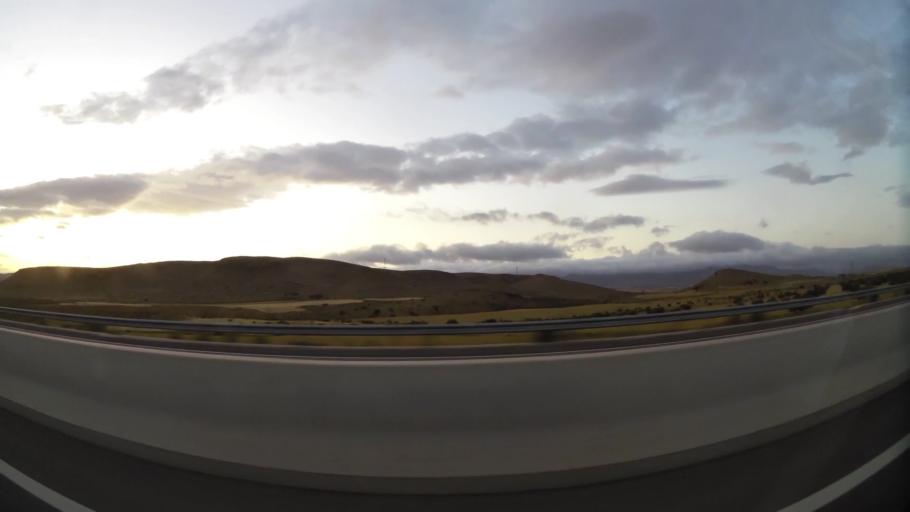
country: MA
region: Oriental
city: El Aioun
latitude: 34.6091
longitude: -2.5627
